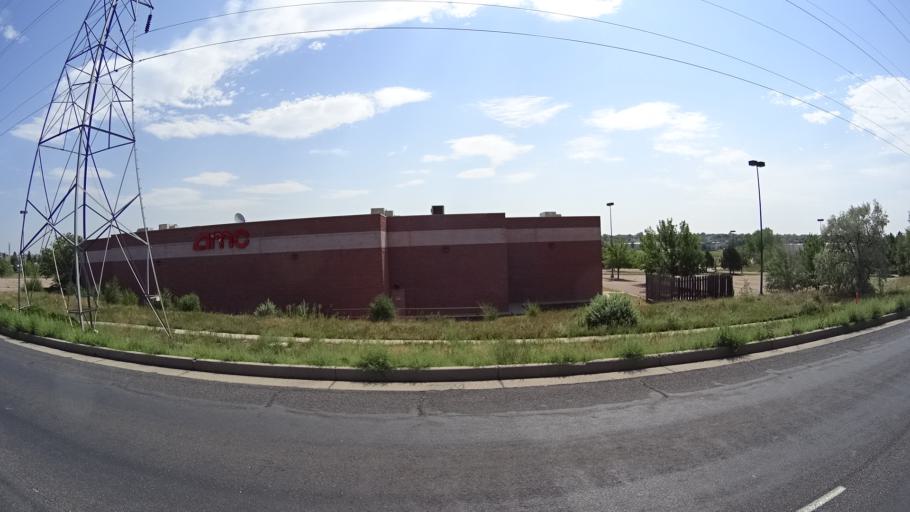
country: US
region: Colorado
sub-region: El Paso County
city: Stratmoor
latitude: 38.8098
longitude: -104.7574
